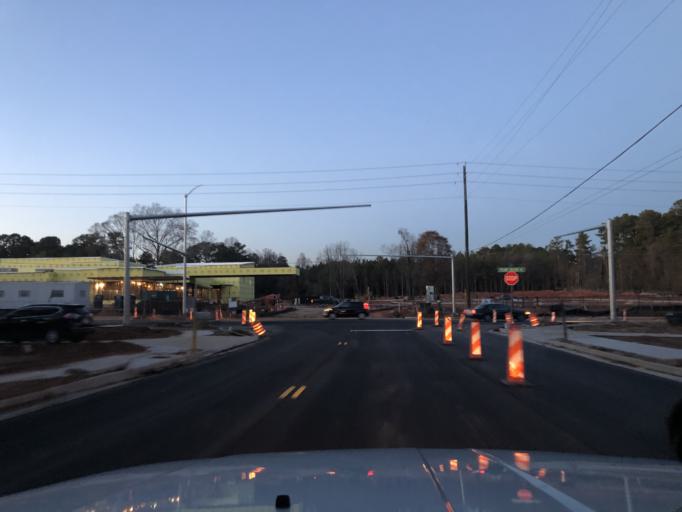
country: US
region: Georgia
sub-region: Clayton County
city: Jonesboro
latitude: 33.5178
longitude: -84.3952
